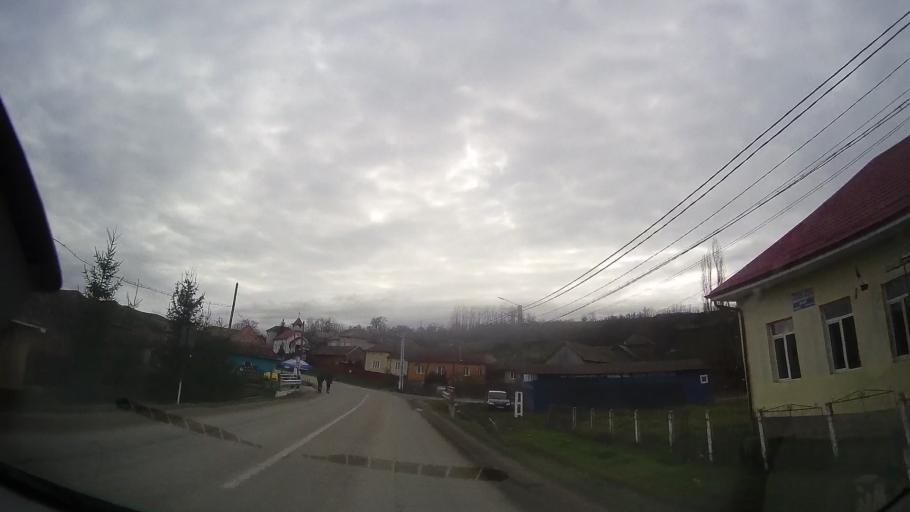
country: RO
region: Bistrita-Nasaud
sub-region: Comuna Budesti
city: Budesti
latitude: 46.8763
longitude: 24.2430
